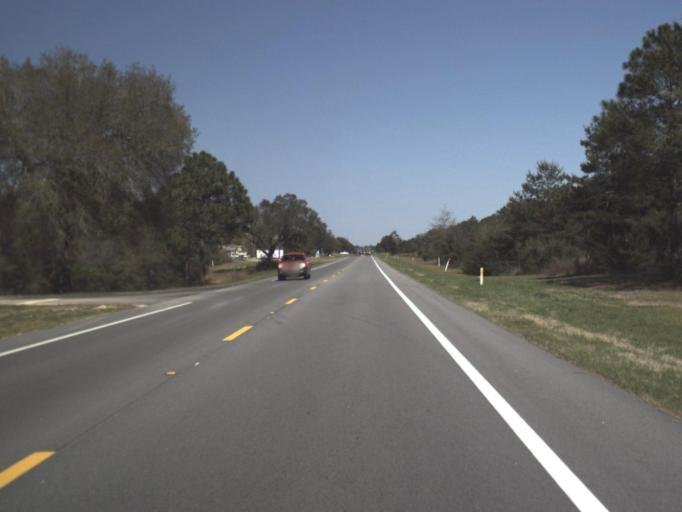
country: US
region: Florida
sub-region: Walton County
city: DeFuniak Springs
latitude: 30.7474
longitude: -86.2988
